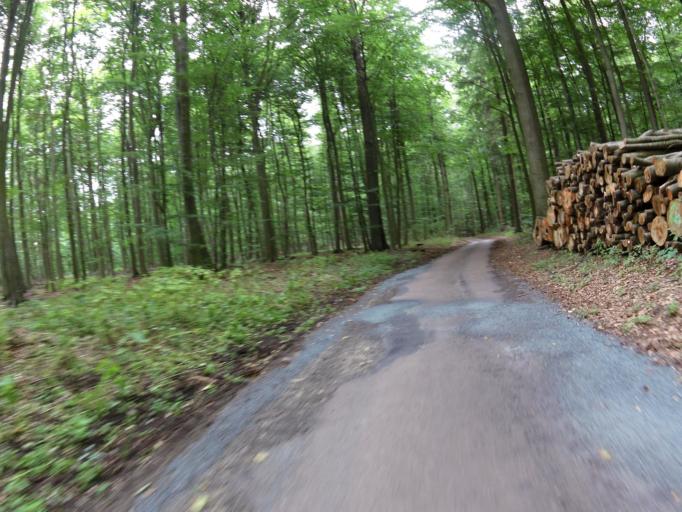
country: DE
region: Mecklenburg-Vorpommern
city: Seebad Heringsdorf
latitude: 53.8963
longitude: 14.1635
